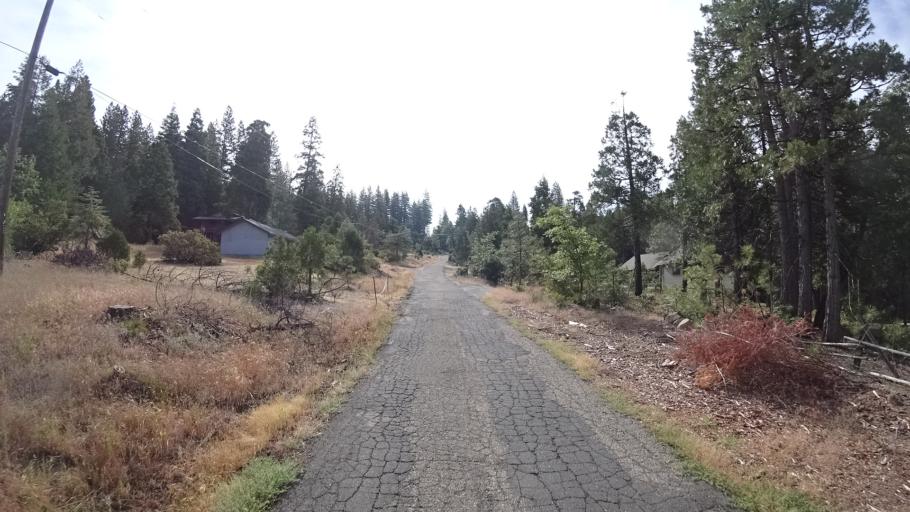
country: US
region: California
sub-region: Calaveras County
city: Arnold
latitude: 38.2672
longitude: -120.3272
